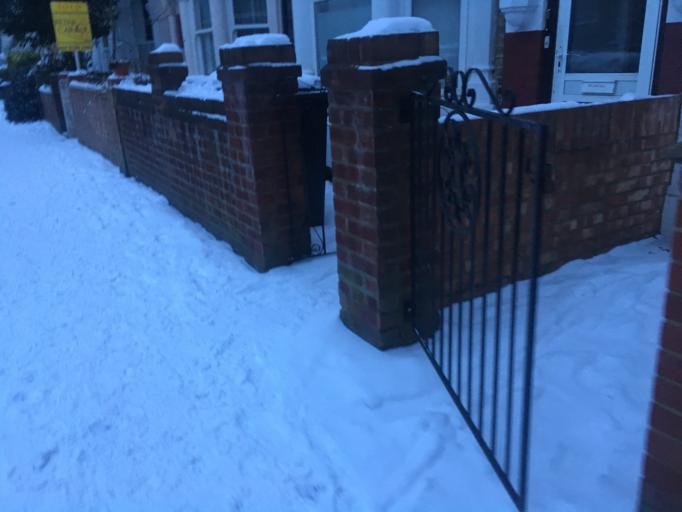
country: GB
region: England
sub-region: Greater London
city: Hammersmith
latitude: 51.5322
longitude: -0.2247
